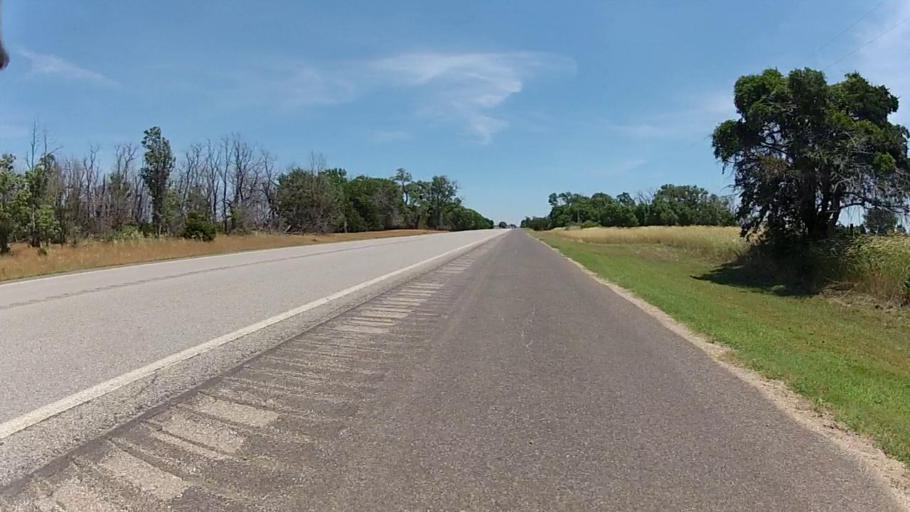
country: US
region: Kansas
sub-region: Barber County
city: Medicine Lodge
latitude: 37.2536
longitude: -98.4070
